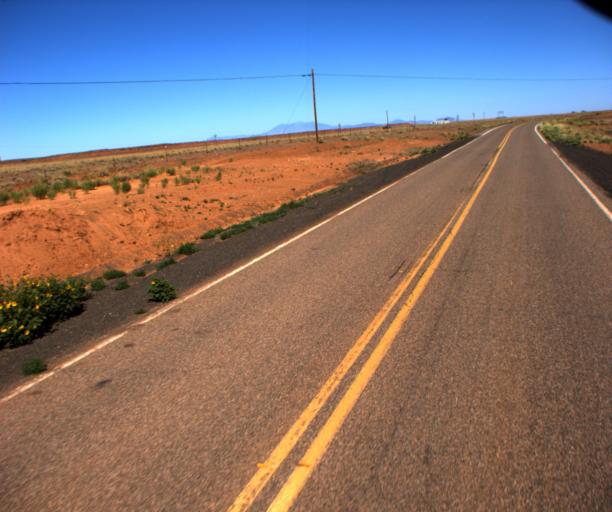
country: US
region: Arizona
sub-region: Coconino County
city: LeChee
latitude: 35.1540
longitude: -110.9019
